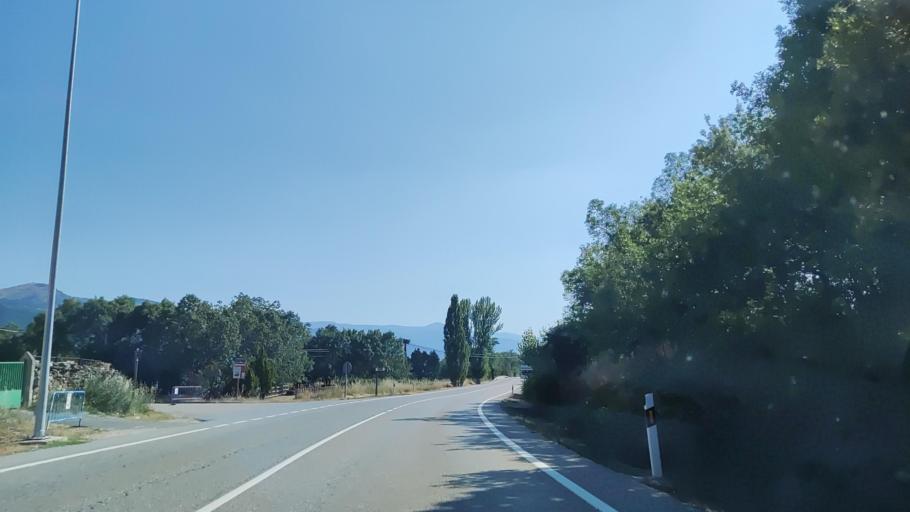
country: ES
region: Madrid
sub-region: Provincia de Madrid
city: Lozoya
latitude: 40.9481
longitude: -3.7929
